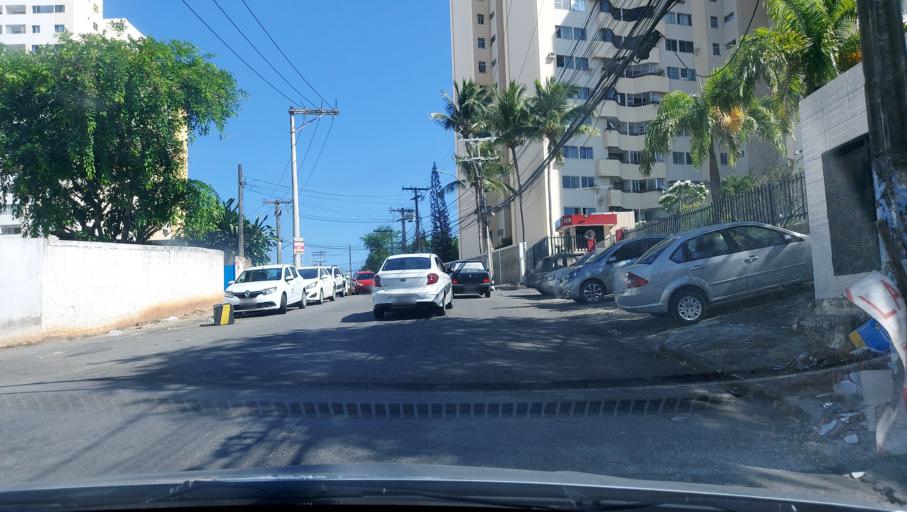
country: BR
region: Bahia
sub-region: Salvador
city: Salvador
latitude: -12.9735
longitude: -38.4357
